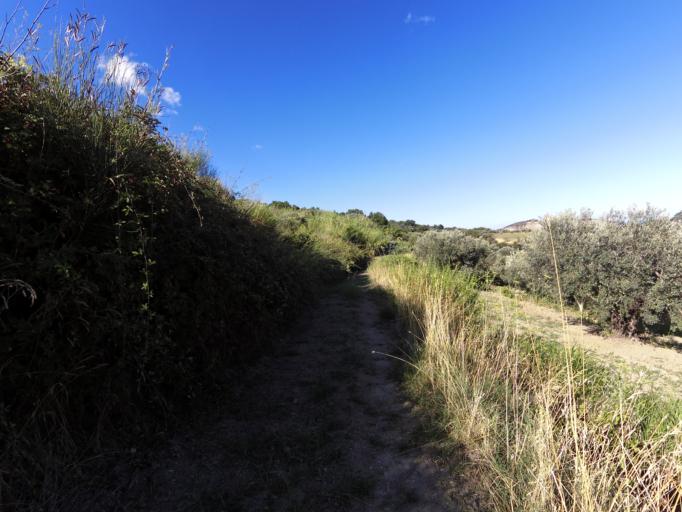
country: IT
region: Calabria
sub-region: Provincia di Reggio Calabria
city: Pazzano
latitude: 38.4446
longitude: 16.4502
